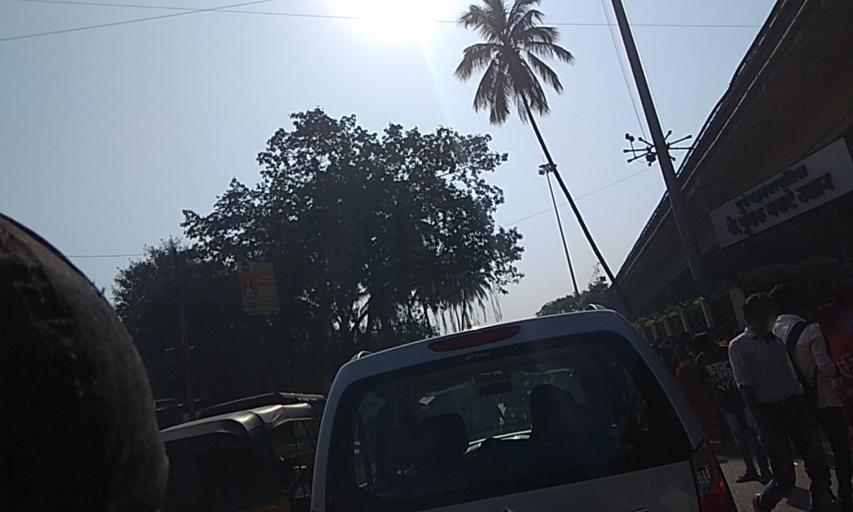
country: IN
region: Maharashtra
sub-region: Pune Division
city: Kharakvasla
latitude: 18.4802
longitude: 73.8047
